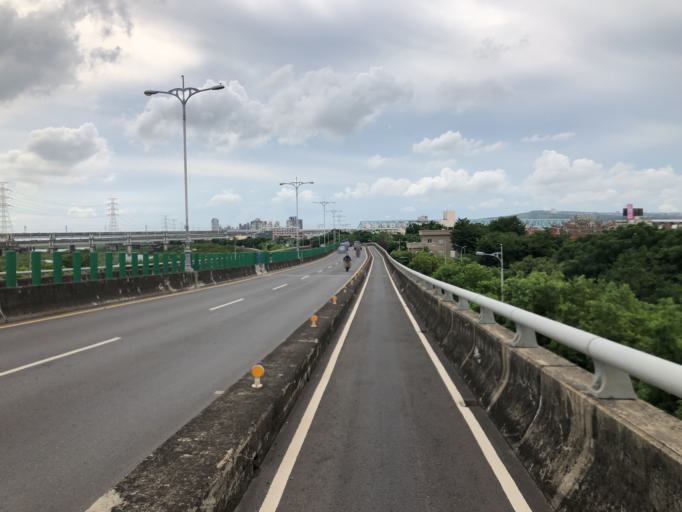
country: TW
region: Taiwan
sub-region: Changhua
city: Chang-hua
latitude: 24.1010
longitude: 120.6229
